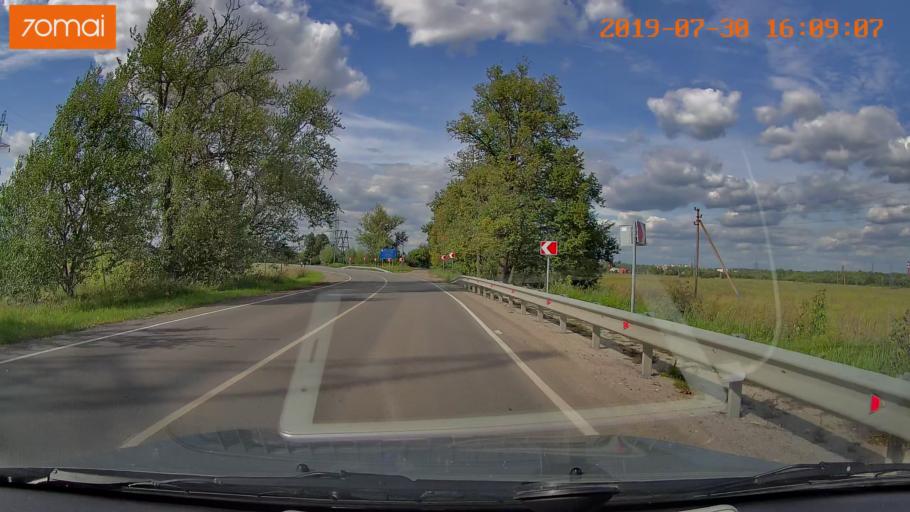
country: RU
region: Moskovskaya
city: Peski
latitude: 55.2508
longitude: 38.7198
